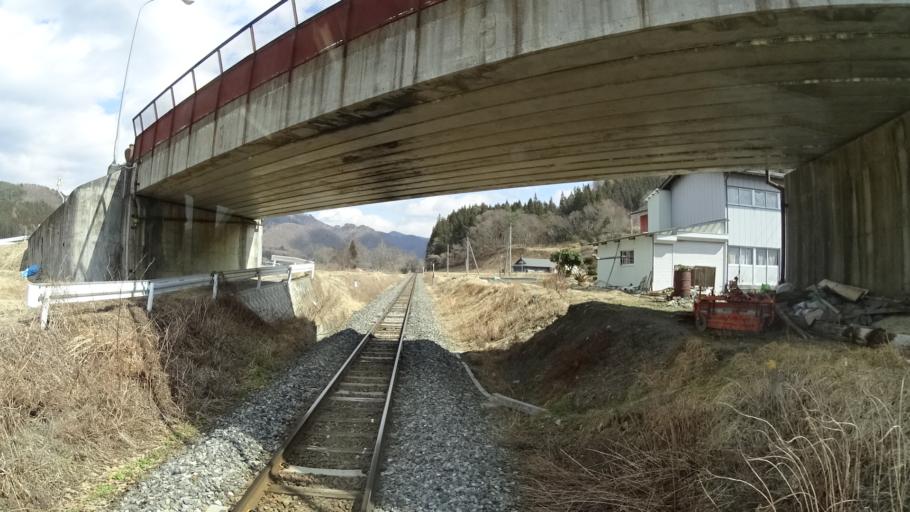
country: JP
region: Iwate
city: Tono
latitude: 39.2643
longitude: 141.5998
